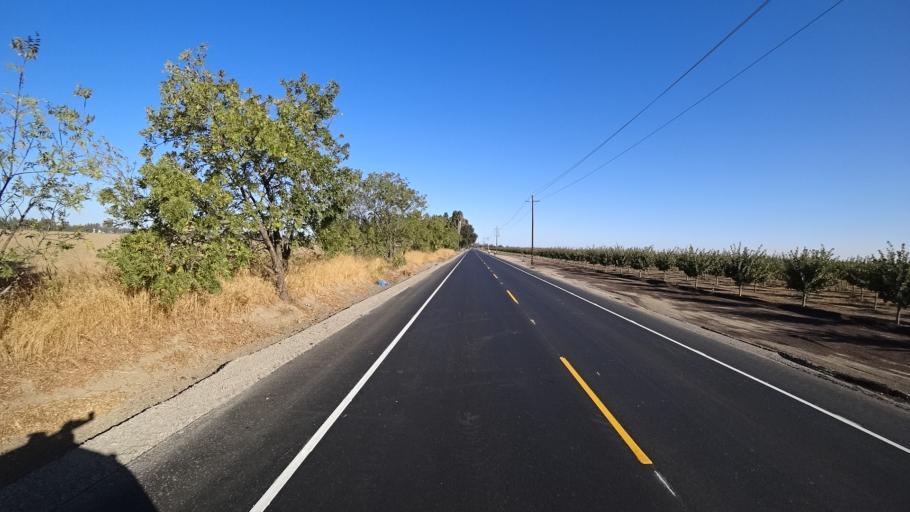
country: US
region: California
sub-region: Yolo County
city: Woodland
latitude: 38.6366
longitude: -121.7847
